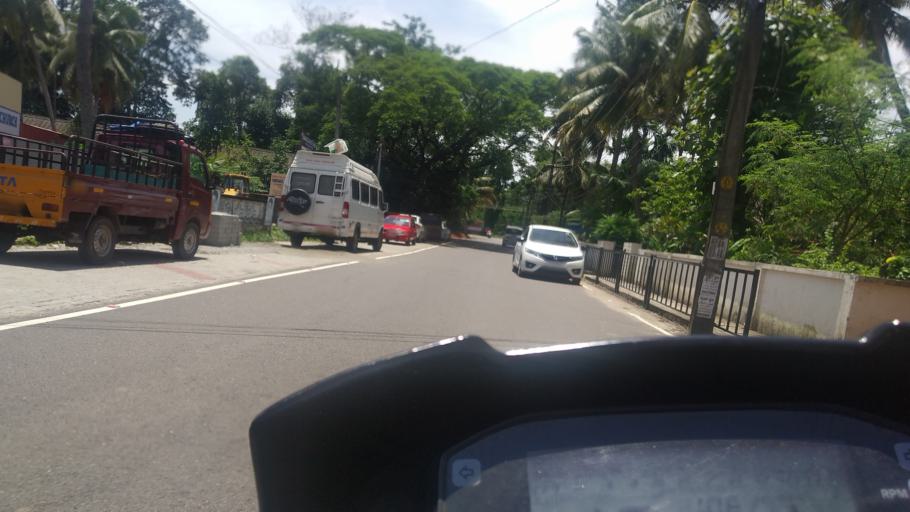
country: IN
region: Kerala
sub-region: Ernakulam
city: Cochin
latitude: 9.9695
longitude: 76.3051
